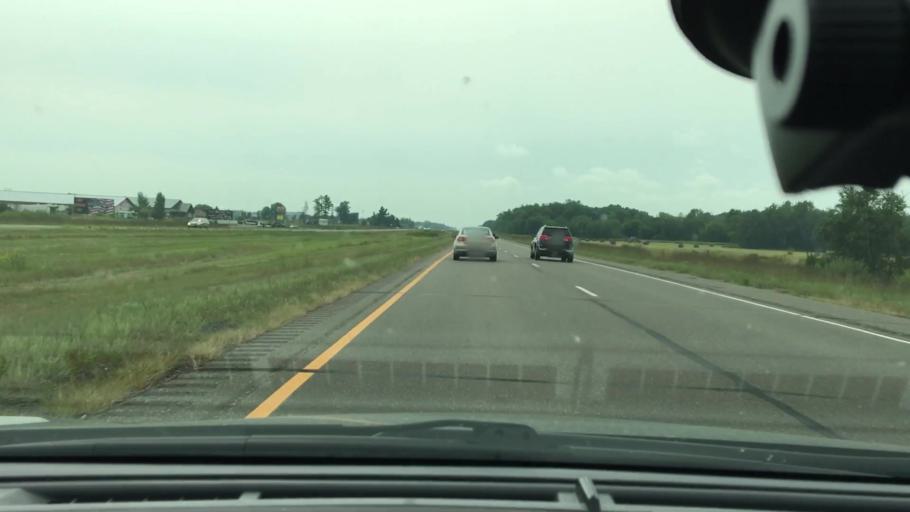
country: US
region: Minnesota
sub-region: Mille Lacs County
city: Vineland
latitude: 46.0421
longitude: -93.6630
